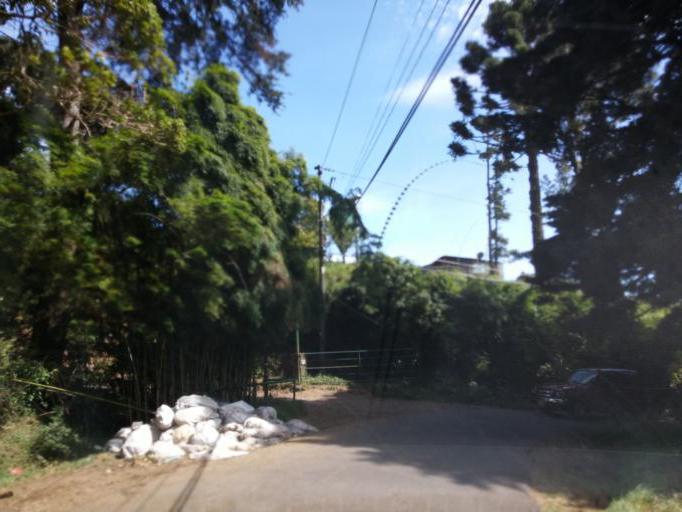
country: CR
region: Heredia
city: Santo Domingo
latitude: 10.1014
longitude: -84.1181
